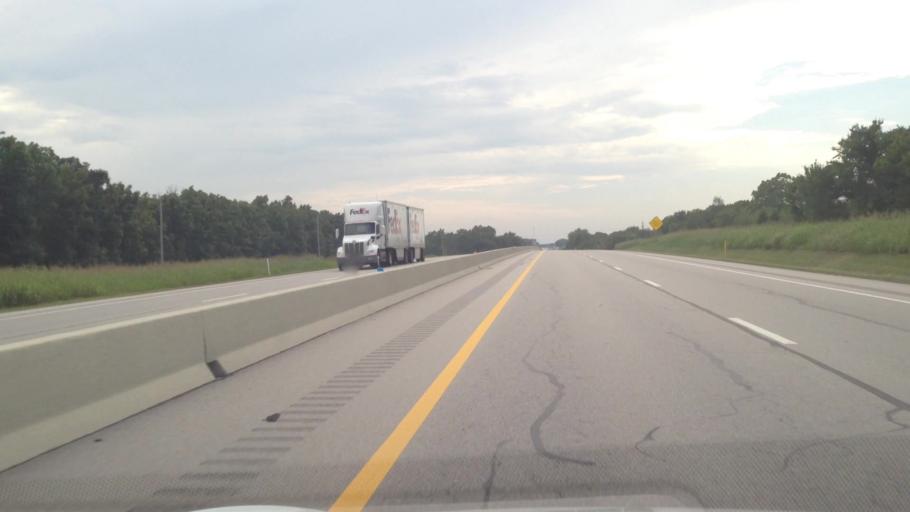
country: US
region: Kansas
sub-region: Cherokee County
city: Baxter Springs
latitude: 36.9242
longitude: -94.7474
